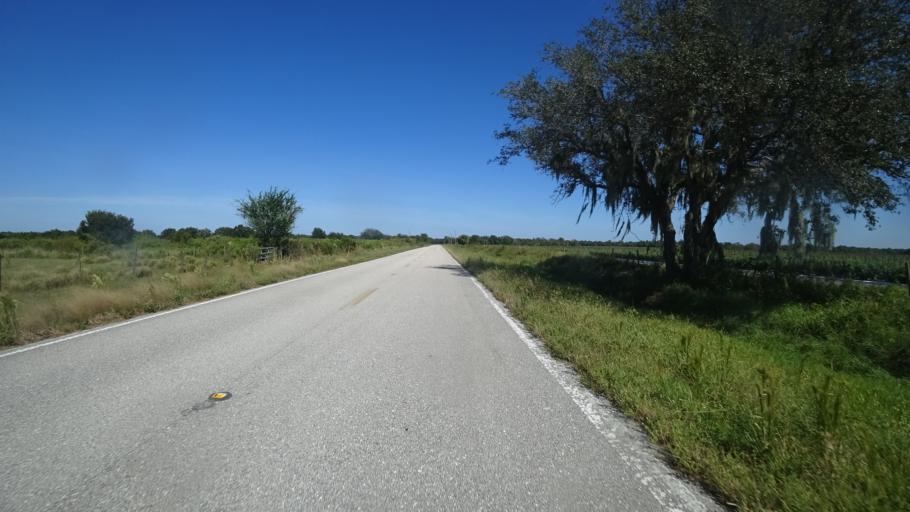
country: US
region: Florida
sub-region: DeSoto County
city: Arcadia
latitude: 27.2841
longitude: -82.0562
